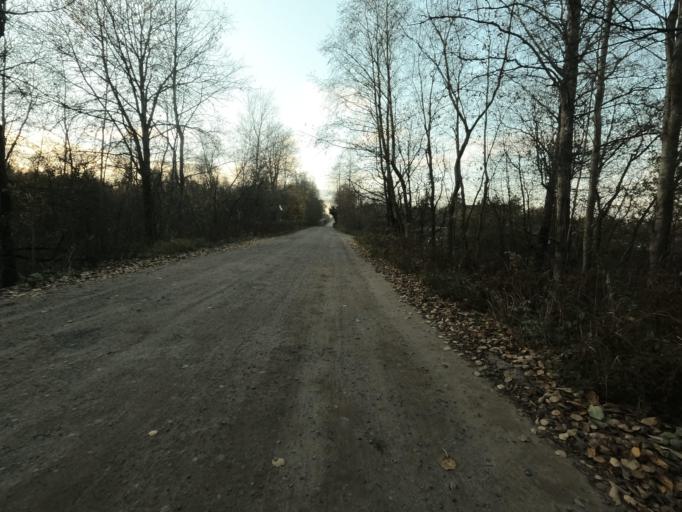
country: RU
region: Leningrad
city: Mga
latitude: 59.7637
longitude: 31.2511
